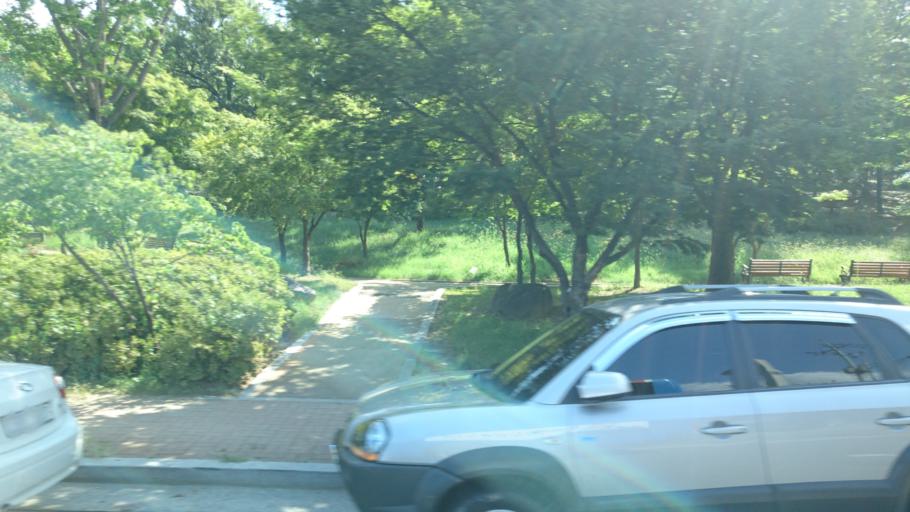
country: KR
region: Daegu
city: Daegu
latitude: 35.8772
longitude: 128.6557
